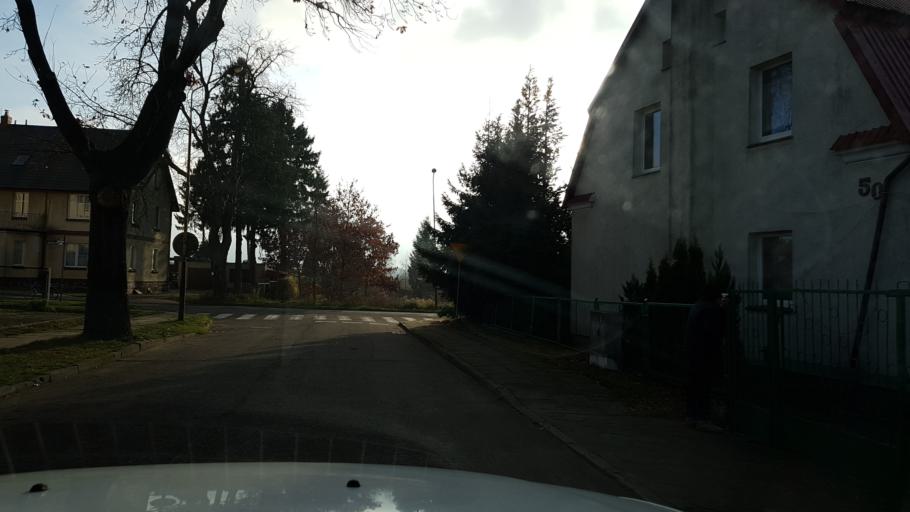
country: PL
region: West Pomeranian Voivodeship
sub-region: Powiat stargardzki
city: Insko
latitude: 53.4376
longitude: 15.5378
